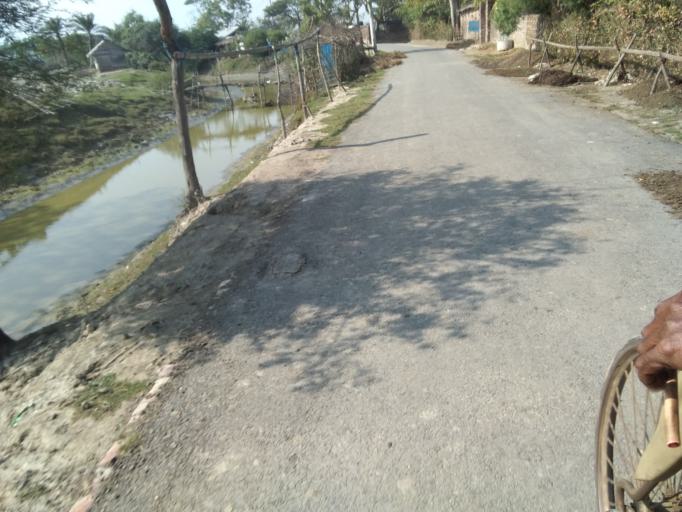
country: BD
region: Khulna
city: Satkhira
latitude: 22.6332
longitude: 89.0184
